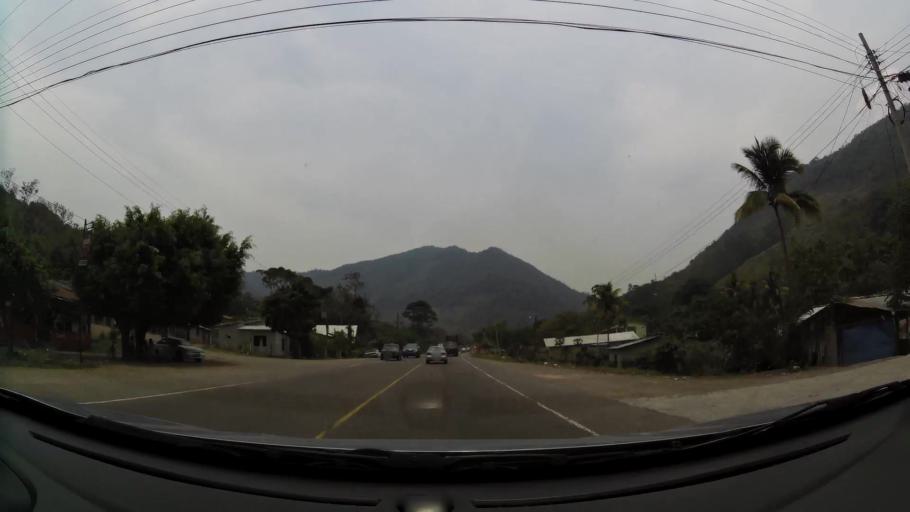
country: HN
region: Comayagua
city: Taulabe
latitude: 14.7337
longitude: -87.9644
